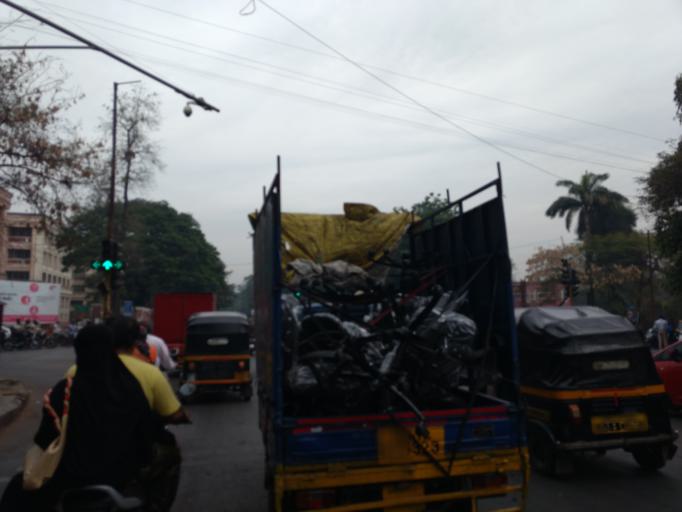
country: IN
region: Maharashtra
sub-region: Pune Division
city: Pune
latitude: 18.5244
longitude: 73.8786
